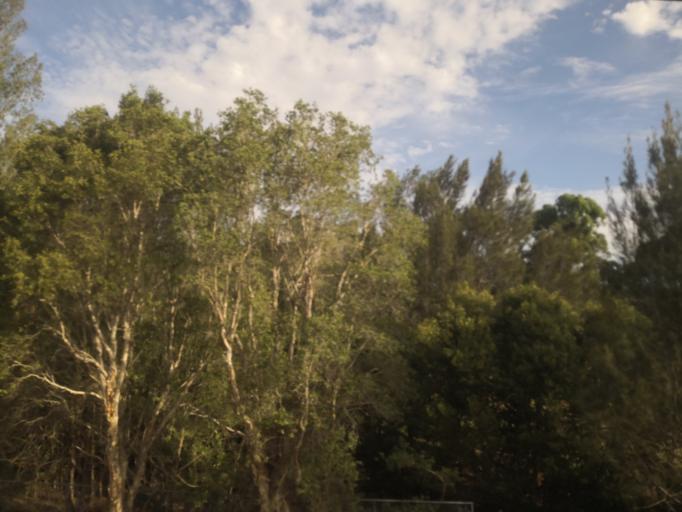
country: AU
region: New South Wales
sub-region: Gosford Shire
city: Blackwall
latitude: -33.4973
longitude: 151.3048
